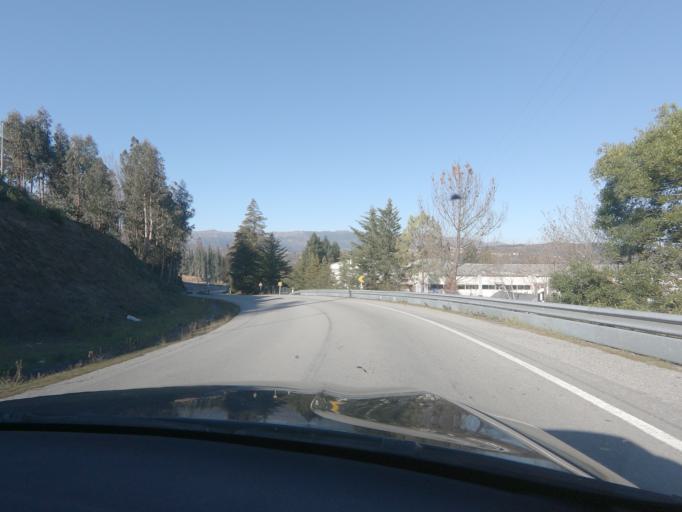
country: PT
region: Viseu
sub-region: Vouzela
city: Vouzela
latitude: 40.7265
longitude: -8.1251
